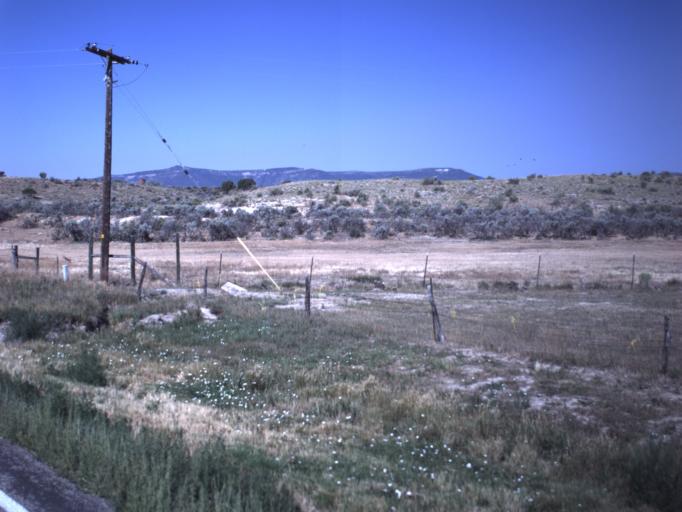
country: US
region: Utah
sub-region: Sanpete County
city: Moroni
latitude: 39.5432
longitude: -111.5308
